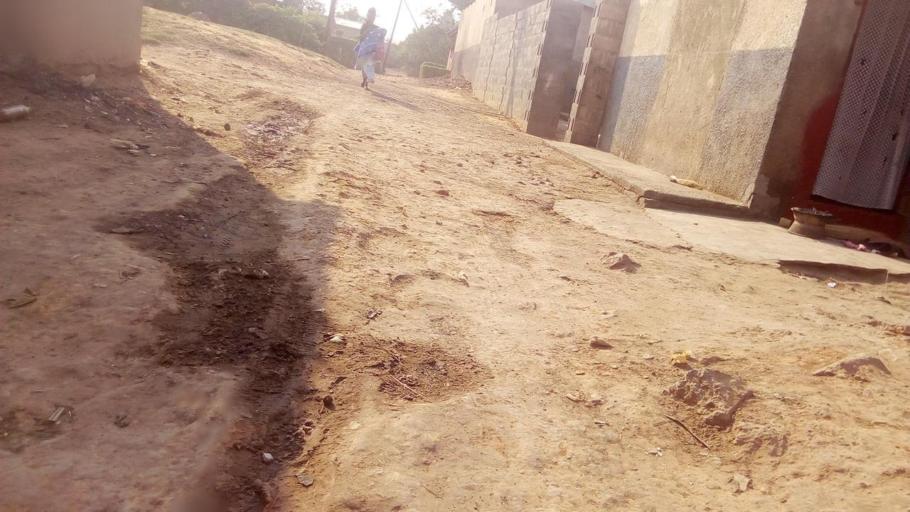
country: ZM
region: Lusaka
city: Lusaka
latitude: -15.3606
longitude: 28.2901
